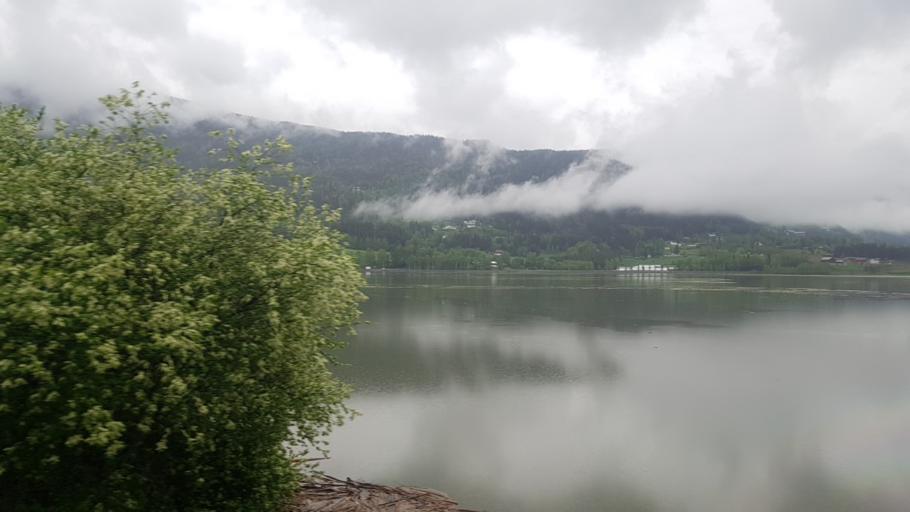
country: NO
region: Oppland
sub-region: Oyer
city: Tretten
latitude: 61.3822
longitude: 10.2599
